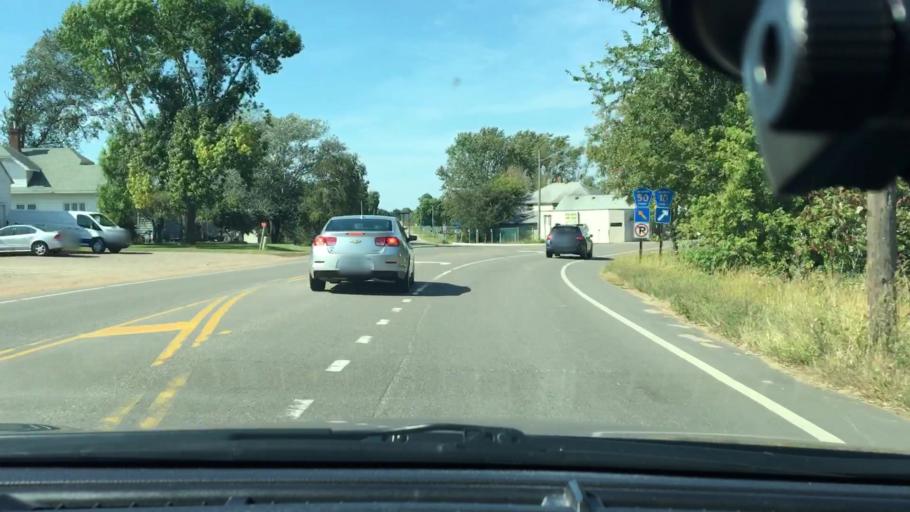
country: US
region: Minnesota
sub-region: Hennepin County
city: Corcoran
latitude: 45.0949
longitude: -93.5473
